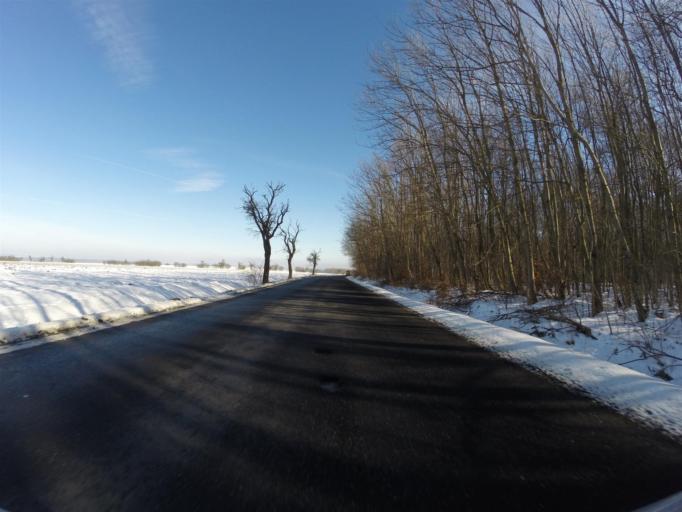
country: DE
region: Thuringia
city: Dobritschen
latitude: 50.9184
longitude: 11.4915
